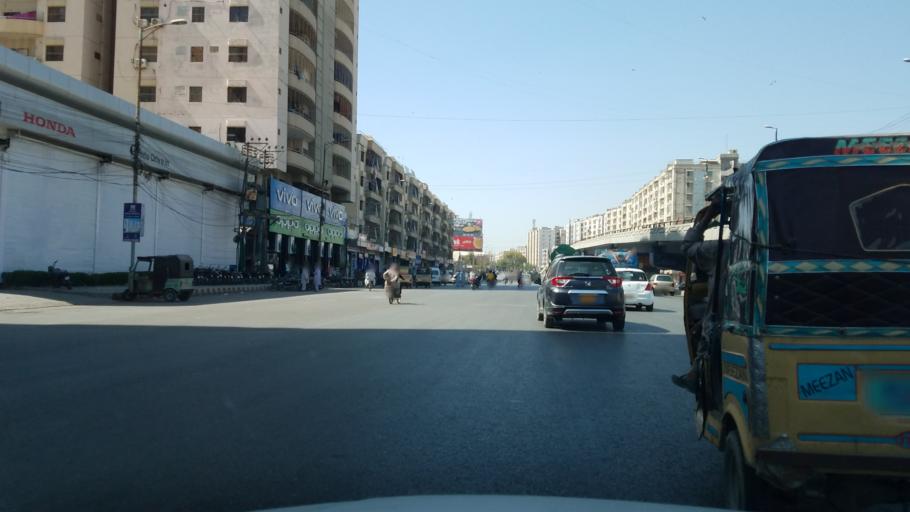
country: PK
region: Sindh
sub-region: Karachi District
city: Karachi
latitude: 24.9033
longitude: 67.1143
